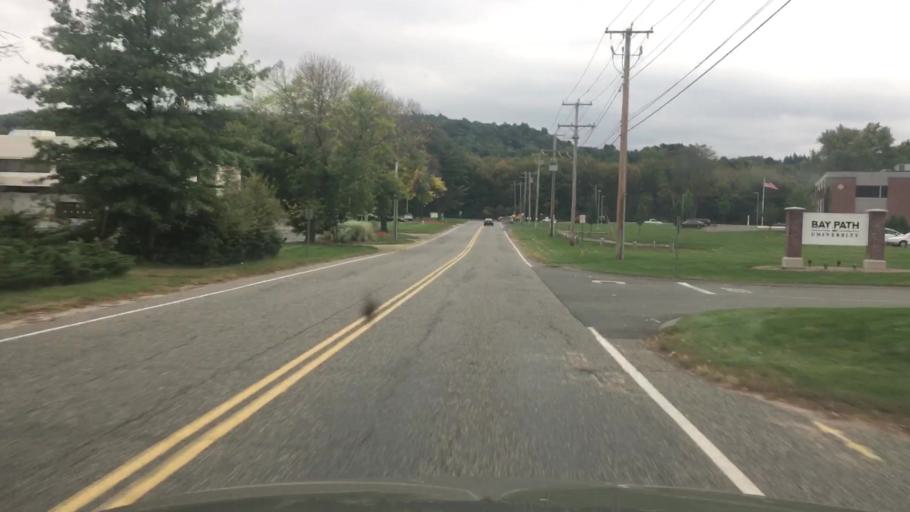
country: US
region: Massachusetts
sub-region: Hampden County
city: East Longmeadow
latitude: 42.0417
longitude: -72.5210
